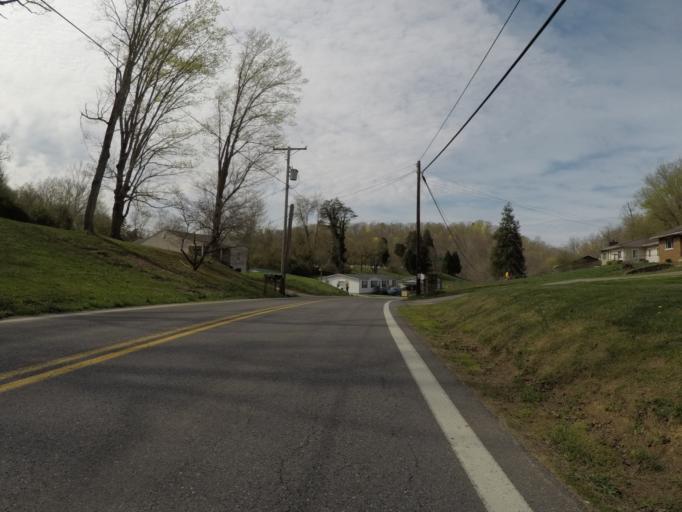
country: US
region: West Virginia
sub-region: Cabell County
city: Pea Ridge
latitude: 38.3671
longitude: -82.3729
